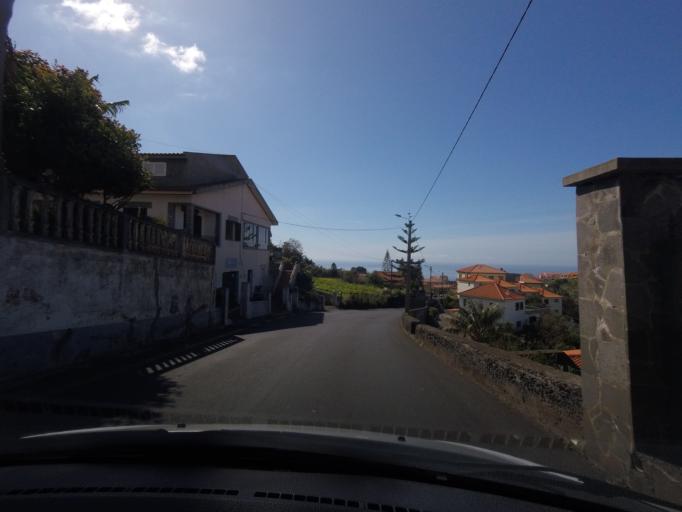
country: PT
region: Madeira
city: Canico
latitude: 32.6527
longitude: -16.8545
